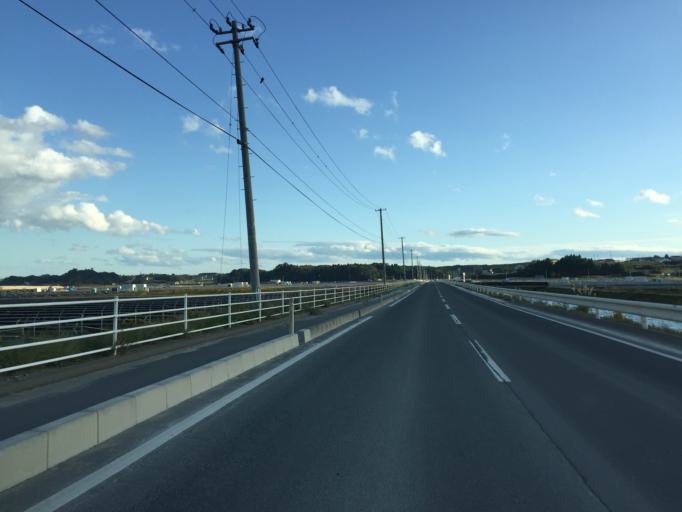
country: JP
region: Miyagi
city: Marumori
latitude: 37.7745
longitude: 140.9808
